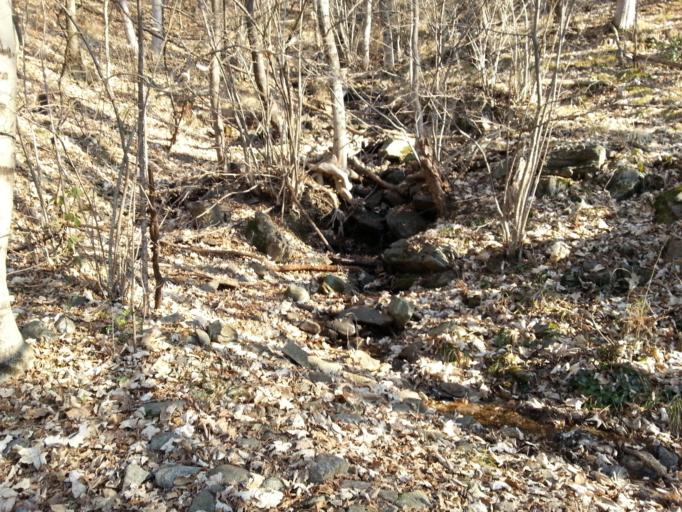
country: CH
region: Ticino
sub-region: Bellinzona District
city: Cadenazzo
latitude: 46.1262
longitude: 8.9267
